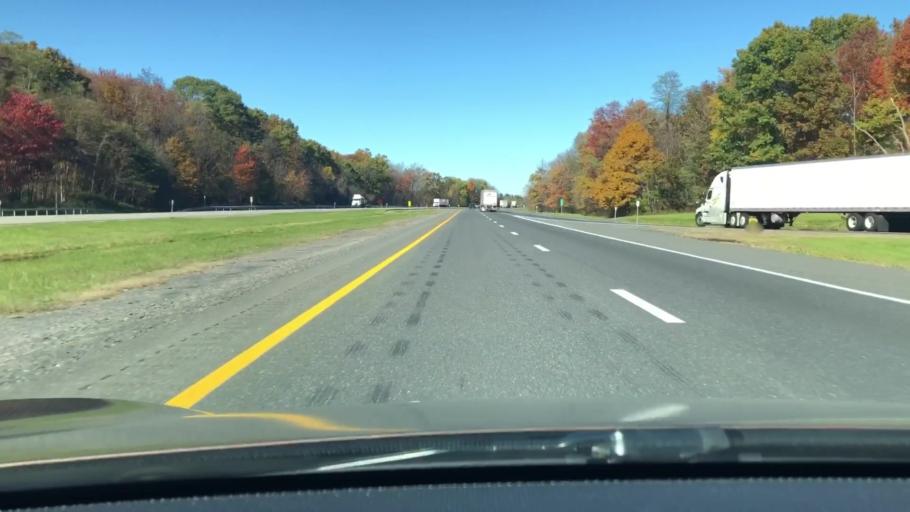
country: US
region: New York
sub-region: Ulster County
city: Plattekill
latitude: 41.5790
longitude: -74.0867
